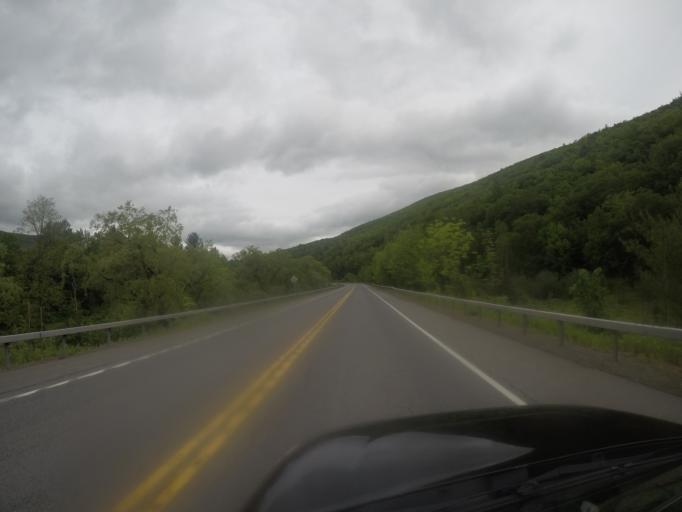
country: US
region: New York
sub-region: Ulster County
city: Shokan
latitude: 42.0893
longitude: -74.3328
